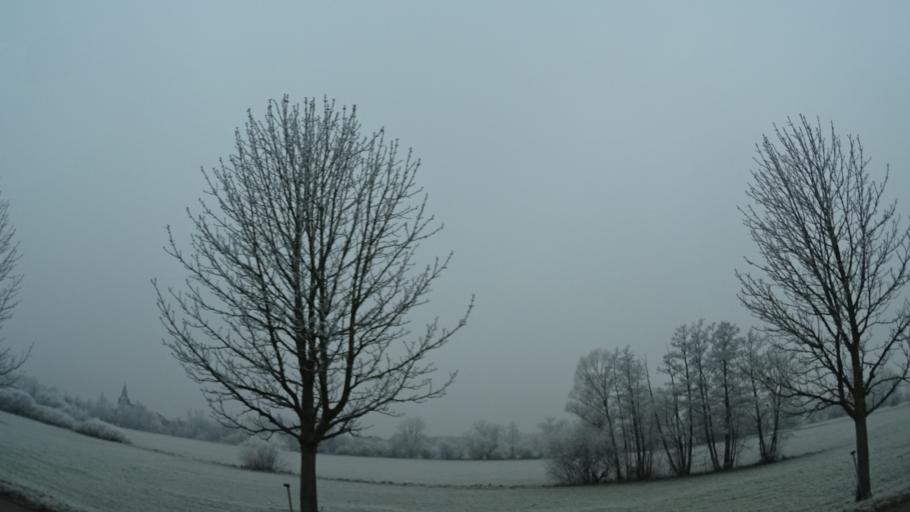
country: DE
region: Bavaria
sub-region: Regierungsbezirk Unterfranken
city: Hassfurt
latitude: 50.0565
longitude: 10.5245
